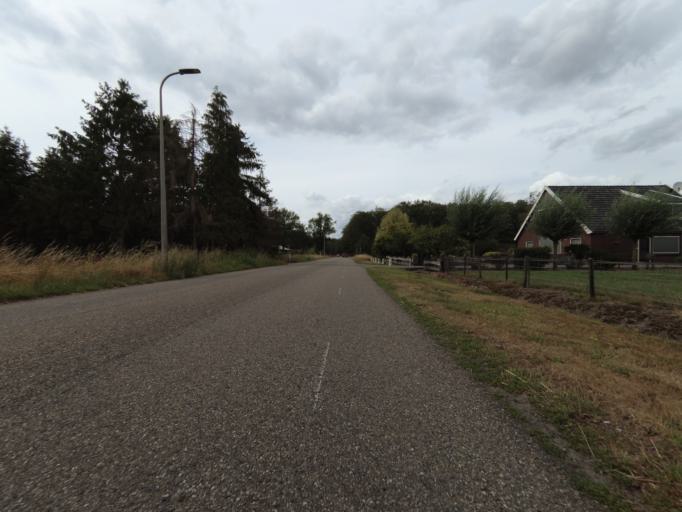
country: NL
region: Overijssel
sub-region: Gemeente Enschede
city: Enschede
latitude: 52.2607
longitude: 6.8836
